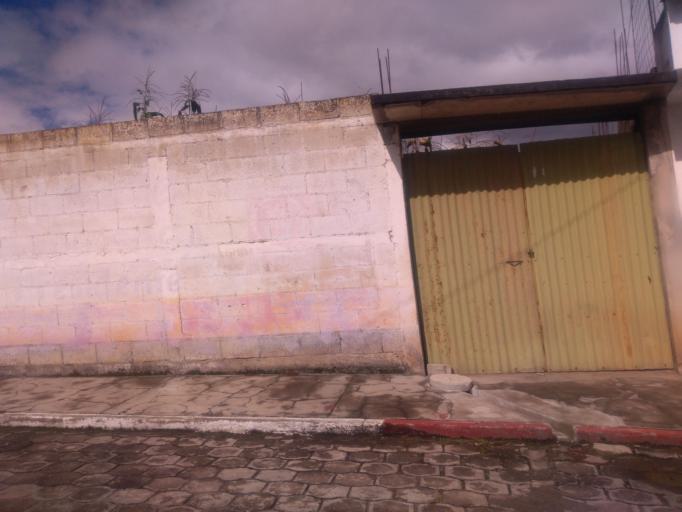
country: GT
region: Quetzaltenango
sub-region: Municipio de La Esperanza
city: La Esperanza
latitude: 14.8678
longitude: -91.5657
